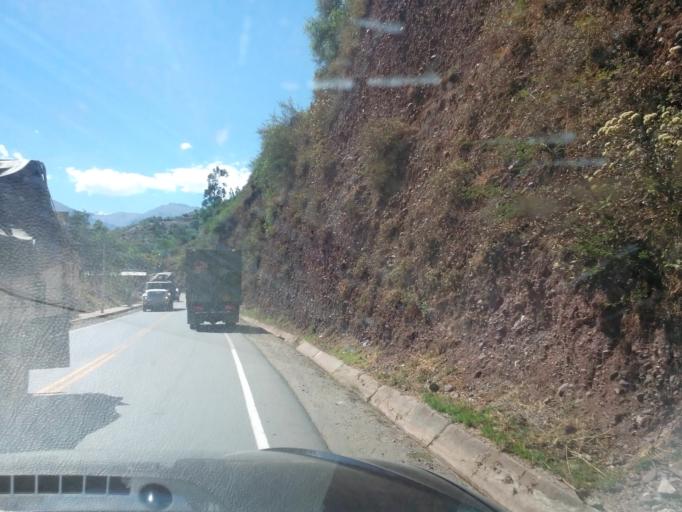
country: PE
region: Cusco
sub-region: Provincia de Anta
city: Limatambo
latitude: -13.4778
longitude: -72.4417
